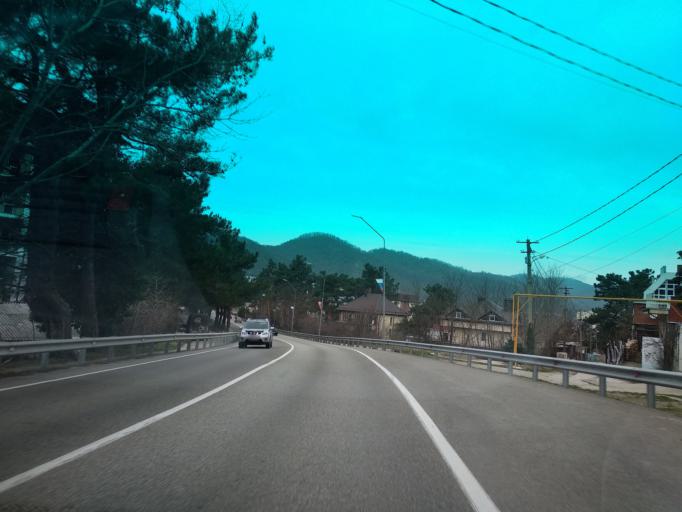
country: RU
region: Krasnodarskiy
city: Ol'ginka
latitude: 44.1968
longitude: 38.8915
